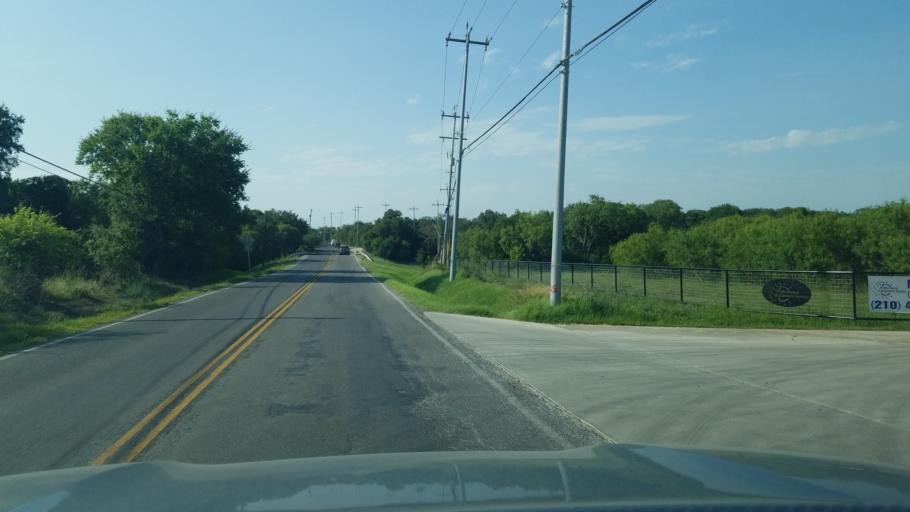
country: US
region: Texas
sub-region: Bexar County
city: Leon Valley
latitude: 29.4475
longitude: -98.7529
